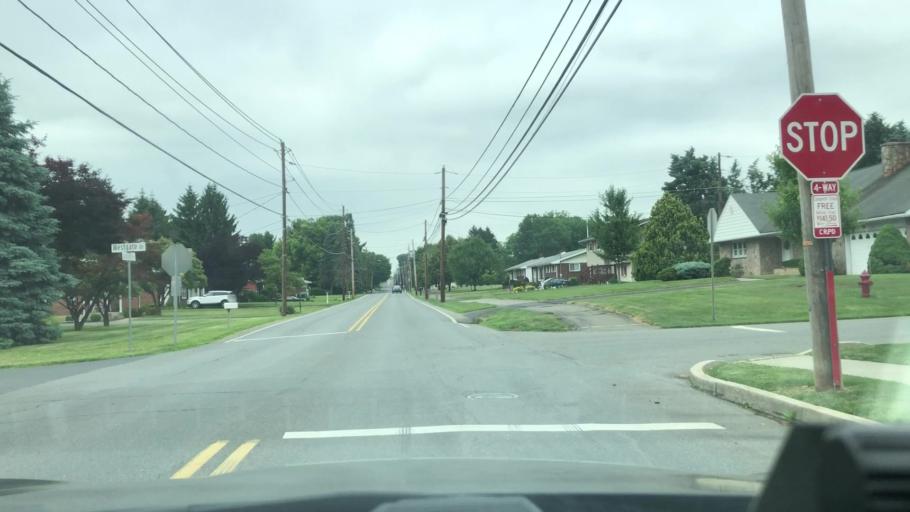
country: US
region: Pennsylvania
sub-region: Northampton County
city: Bethlehem
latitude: 40.6454
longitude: -75.3996
